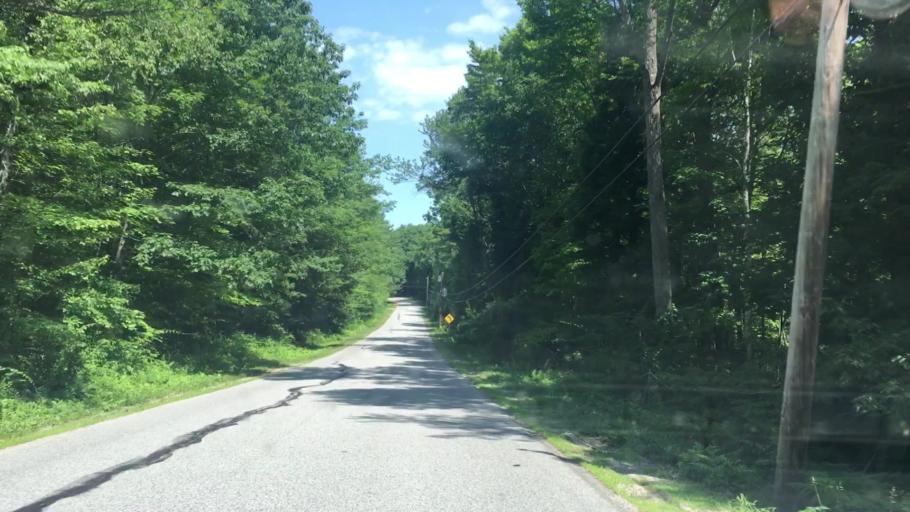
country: US
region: Maine
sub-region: Kennebec County
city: Wayne
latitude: 44.3313
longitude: -70.0582
